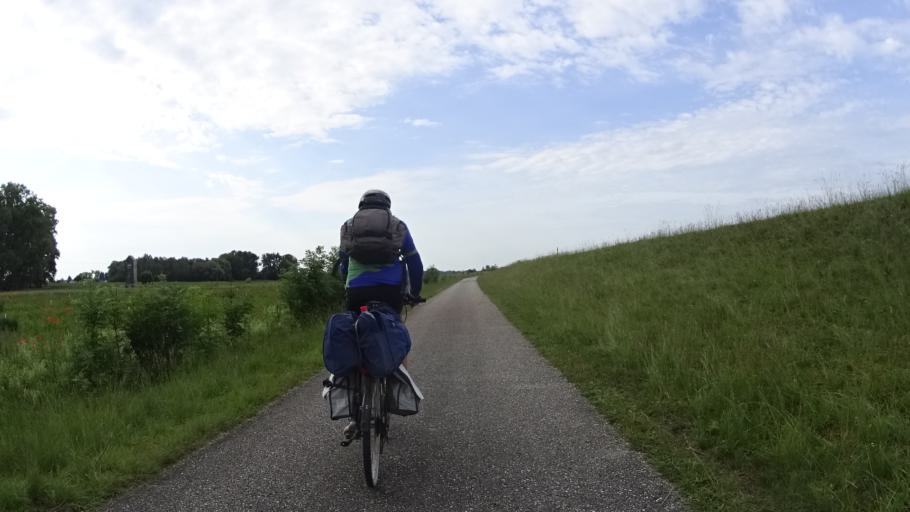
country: DE
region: Bavaria
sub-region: Lower Bavaria
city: Irlbach
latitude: 48.8636
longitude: 12.7627
